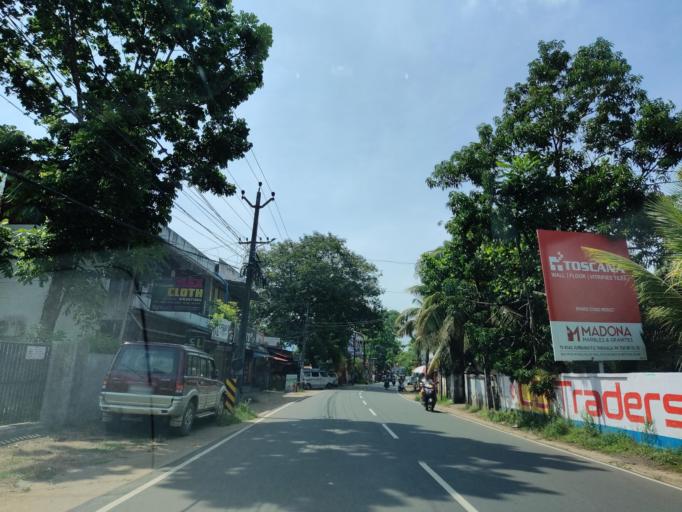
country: IN
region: Kerala
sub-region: Alappuzha
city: Mavelikara
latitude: 9.3068
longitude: 76.5342
